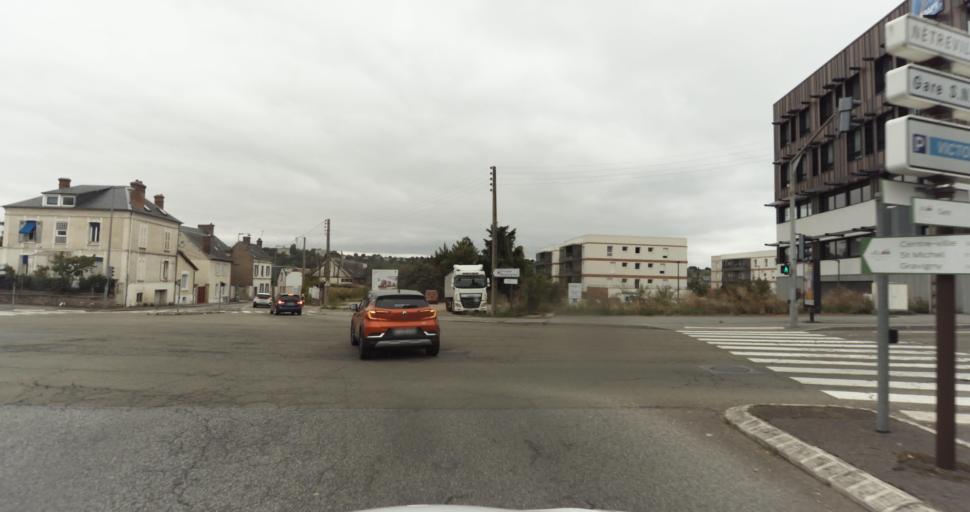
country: FR
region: Haute-Normandie
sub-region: Departement de l'Eure
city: Evreux
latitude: 49.0185
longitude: 1.1429
